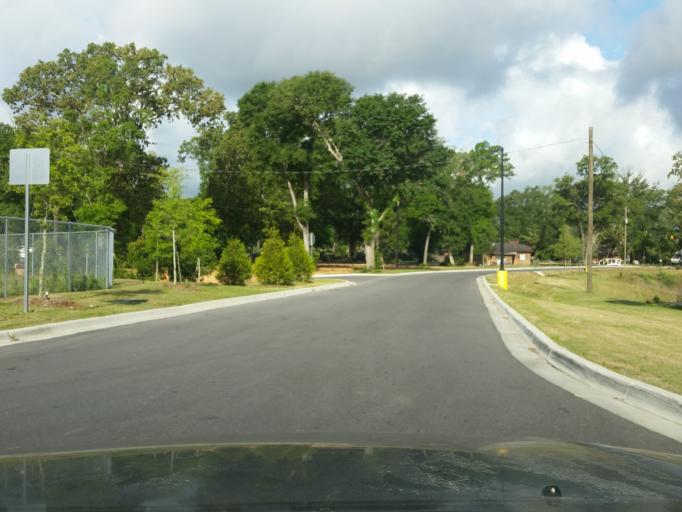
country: US
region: Florida
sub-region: Escambia County
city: Ensley
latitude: 30.5331
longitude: -87.3149
